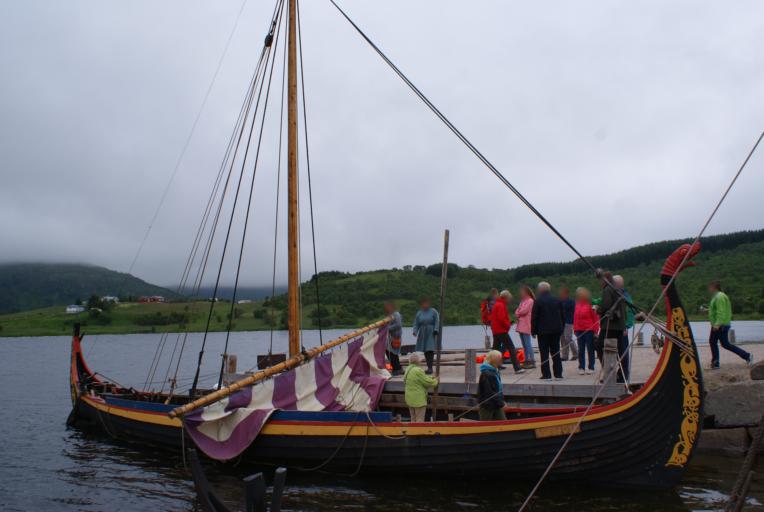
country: NO
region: Nordland
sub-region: Vestvagoy
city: Evjen
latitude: 68.2440
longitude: 13.7855
